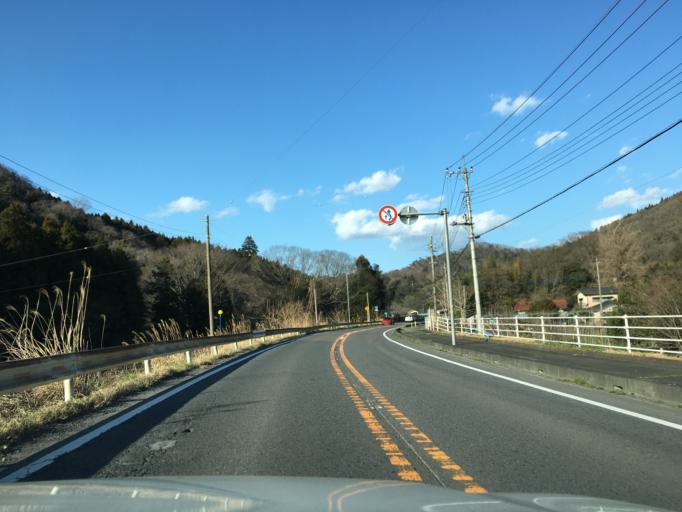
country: JP
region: Ibaraki
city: Daigo
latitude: 36.6833
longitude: 140.3875
